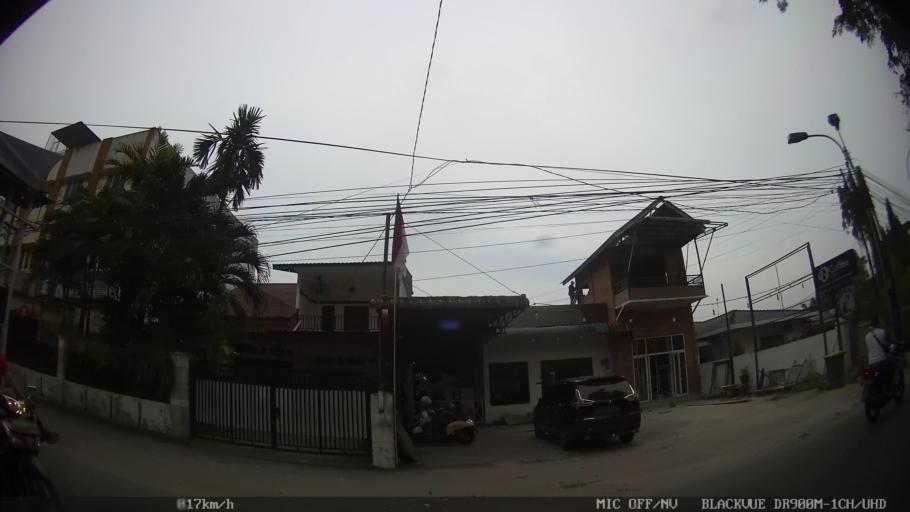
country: ID
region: North Sumatra
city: Medan
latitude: 3.5531
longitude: 98.6918
